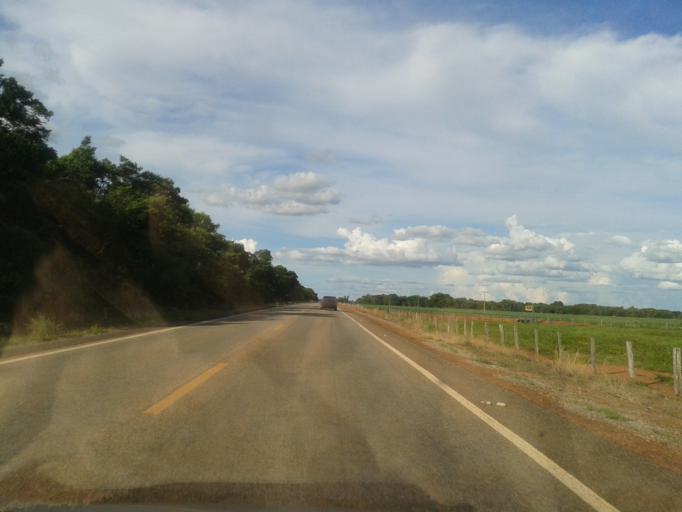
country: BR
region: Goias
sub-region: Mozarlandia
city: Mozarlandia
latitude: -14.3239
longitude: -50.4113
